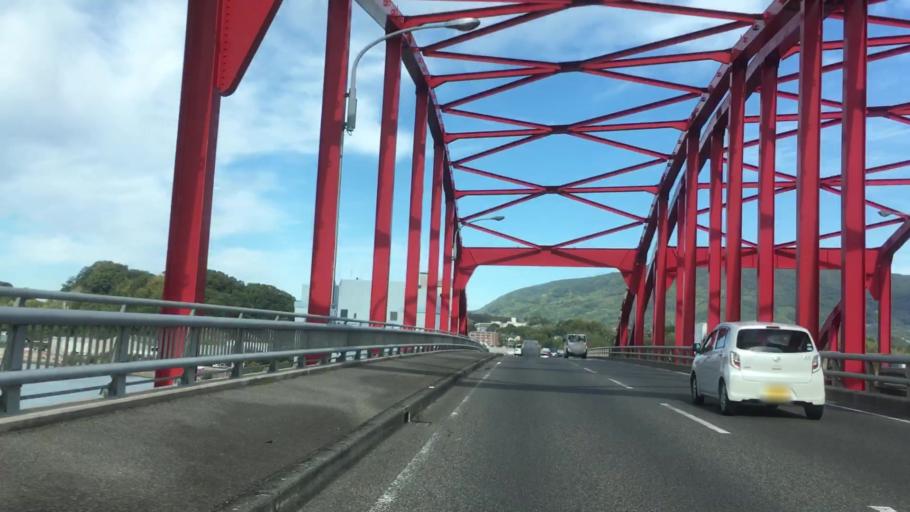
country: JP
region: Nagasaki
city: Sasebo
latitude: 33.1421
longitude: 129.7817
